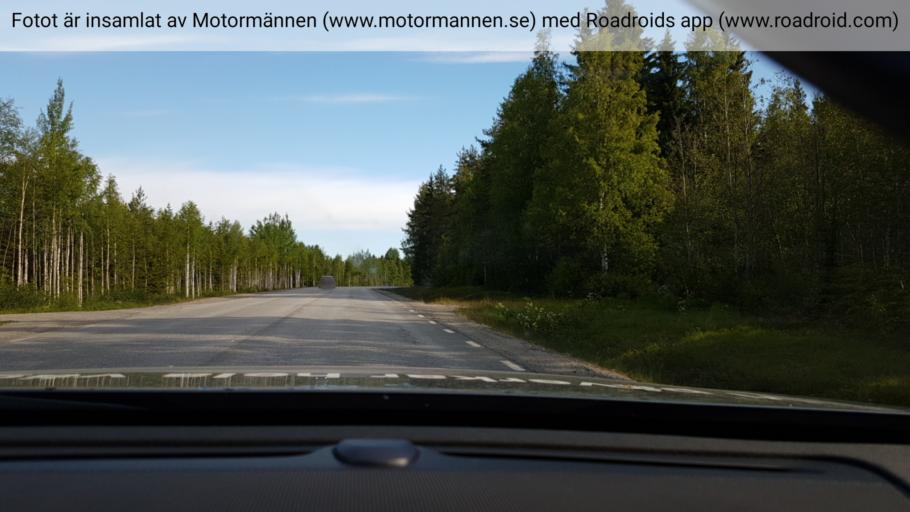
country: SE
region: Vaesterbotten
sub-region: Vannas Kommun
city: Vaennaes
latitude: 63.9319
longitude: 19.7717
